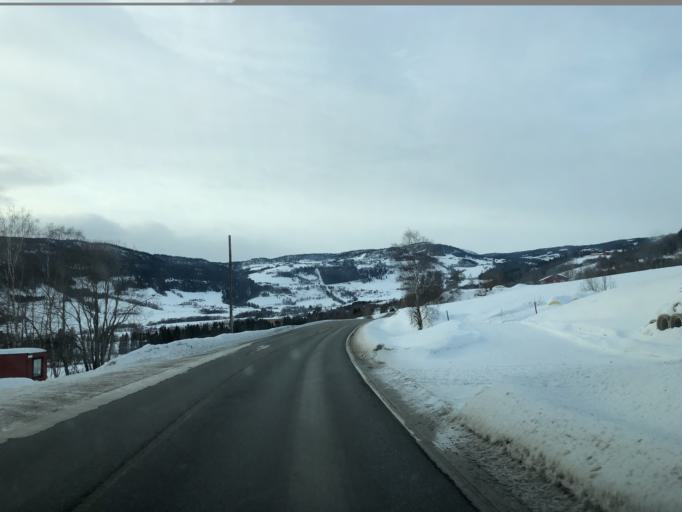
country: NO
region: Oppland
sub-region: Gausdal
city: Segalstad bru
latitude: 61.2563
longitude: 10.1749
